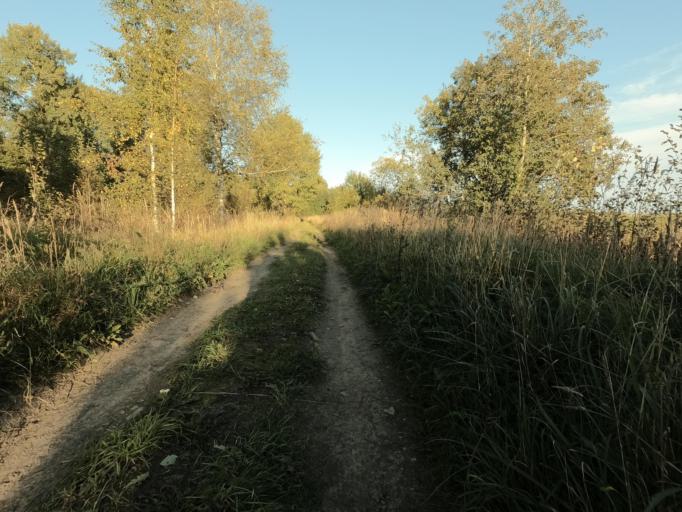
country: RU
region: Leningrad
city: Nikol'skoye
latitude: 59.7006
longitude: 30.7438
